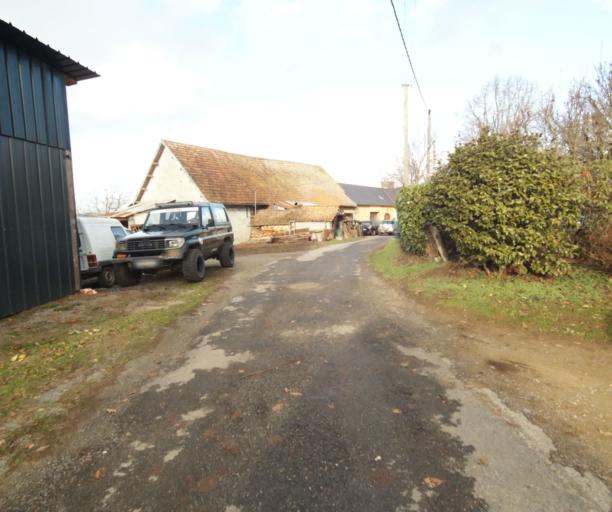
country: FR
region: Limousin
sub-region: Departement de la Correze
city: Laguenne
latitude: 45.2350
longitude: 1.7873
